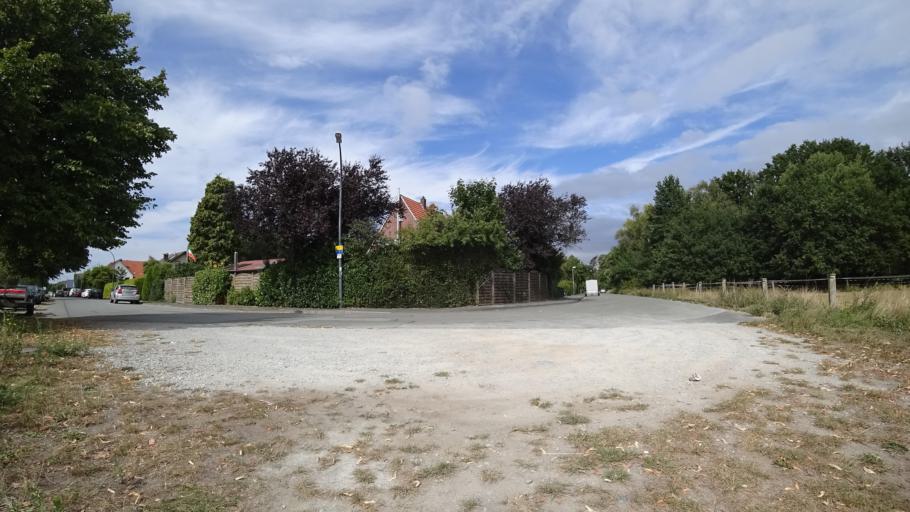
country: DE
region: North Rhine-Westphalia
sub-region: Regierungsbezirk Detmold
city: Guetersloh
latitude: 51.9384
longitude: 8.4547
